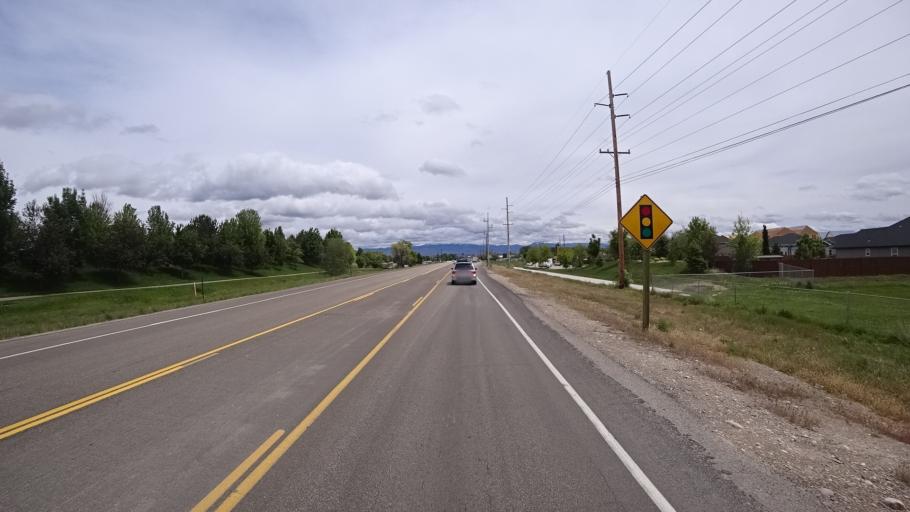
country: US
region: Idaho
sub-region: Ada County
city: Eagle
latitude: 43.6934
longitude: -116.4178
